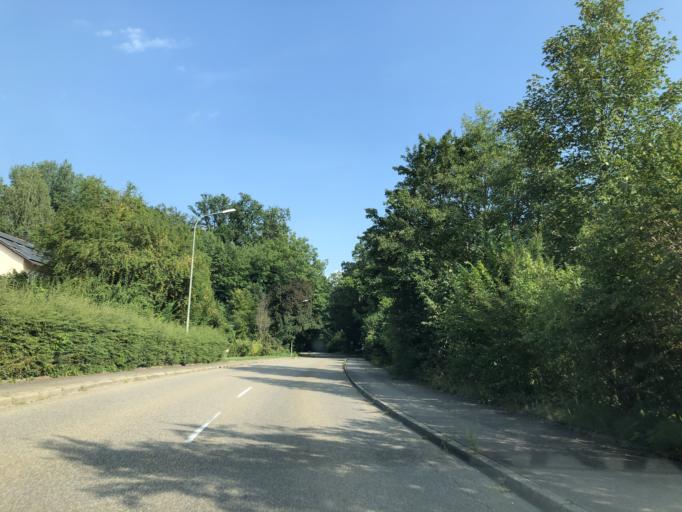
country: DE
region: Baden-Wuerttemberg
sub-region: Freiburg Region
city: Achern
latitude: 48.6270
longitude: 8.0869
